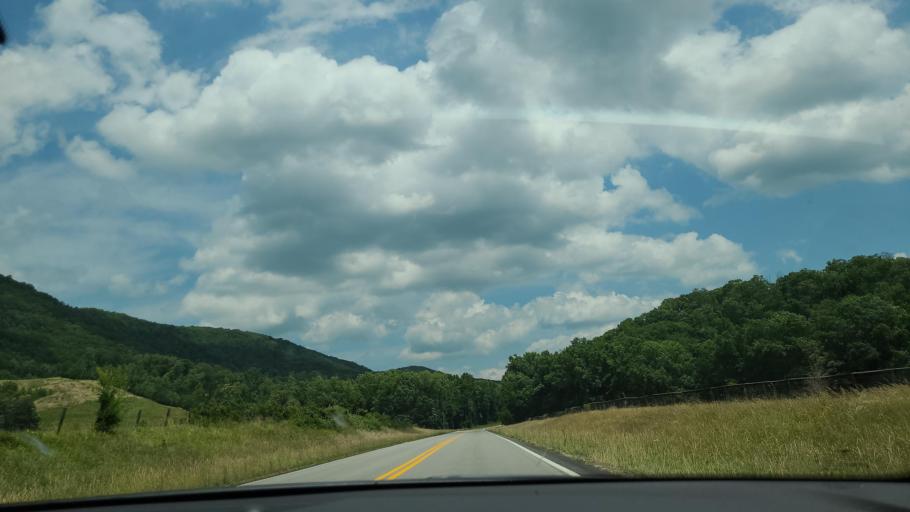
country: US
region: Tennessee
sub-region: Cumberland County
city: Lake Tansi
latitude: 35.7414
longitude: -85.0714
